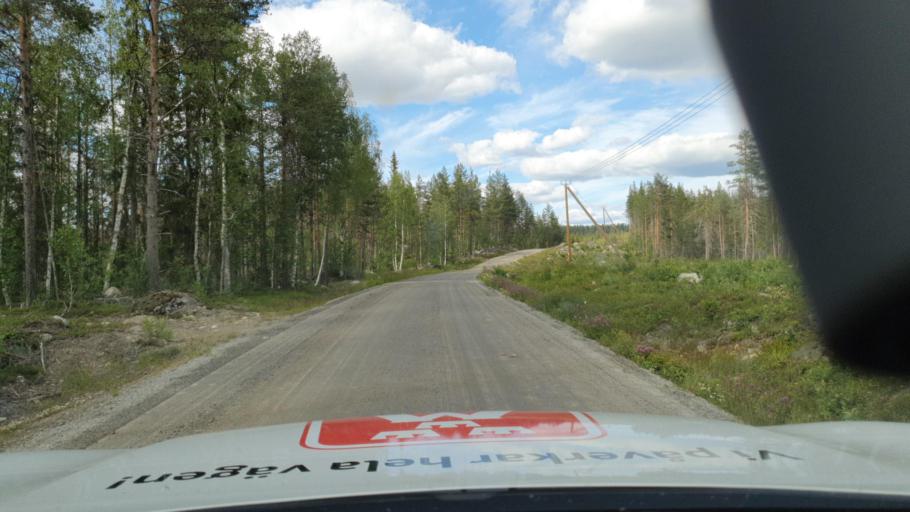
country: SE
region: Vaesterbotten
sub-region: Lycksele Kommun
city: Soderfors
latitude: 64.2779
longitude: 18.1555
